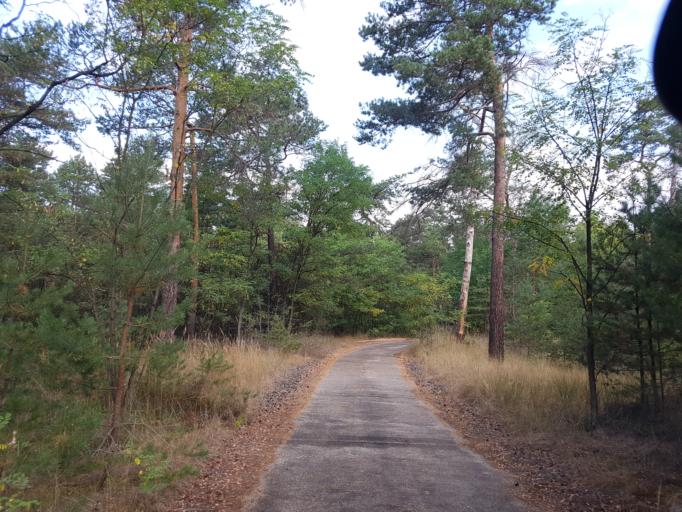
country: DE
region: Brandenburg
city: Finsterwalde
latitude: 51.5979
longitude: 13.7481
